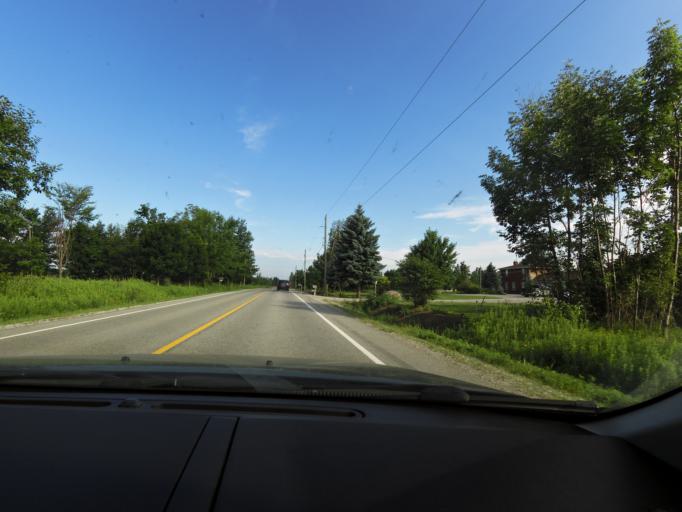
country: CA
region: Ontario
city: Brampton
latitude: 43.8154
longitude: -79.8642
